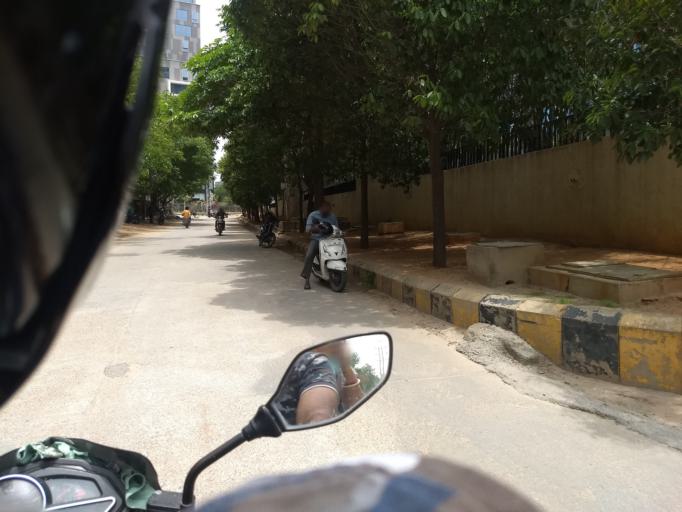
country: IN
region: Telangana
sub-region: Rangareddi
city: Kukatpalli
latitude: 17.4593
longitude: 78.3688
